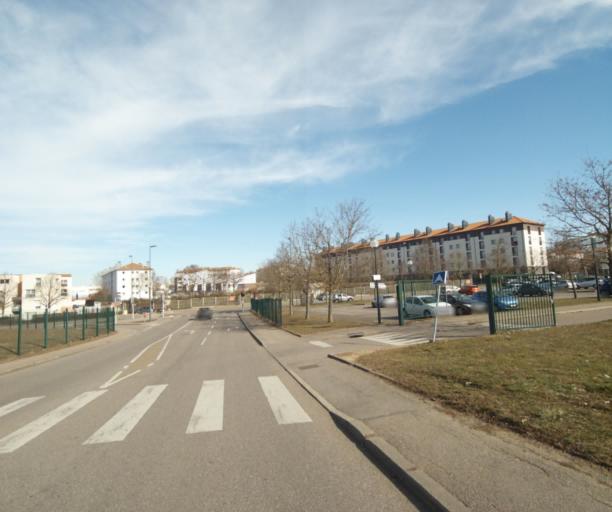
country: FR
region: Lorraine
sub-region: Departement de Meurthe-et-Moselle
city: Villers-les-Nancy
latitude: 48.6683
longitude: 6.1606
